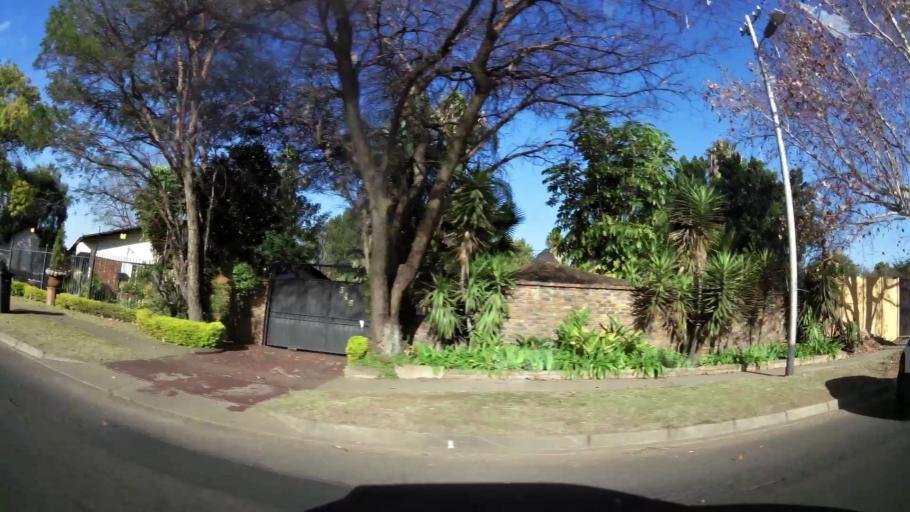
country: ZA
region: Gauteng
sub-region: City of Tshwane Metropolitan Municipality
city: Pretoria
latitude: -25.7235
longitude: 28.2149
